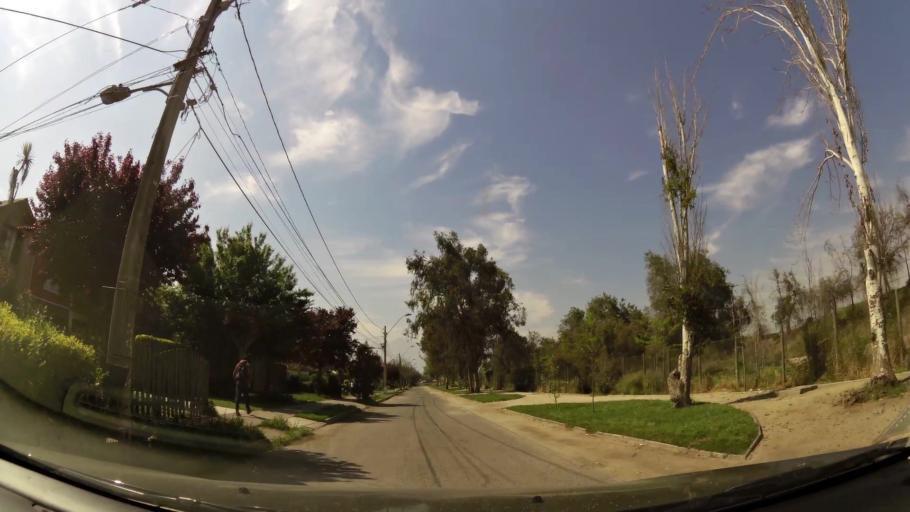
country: CL
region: Santiago Metropolitan
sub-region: Provincia de Santiago
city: La Pintana
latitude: -33.5682
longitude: -70.5965
